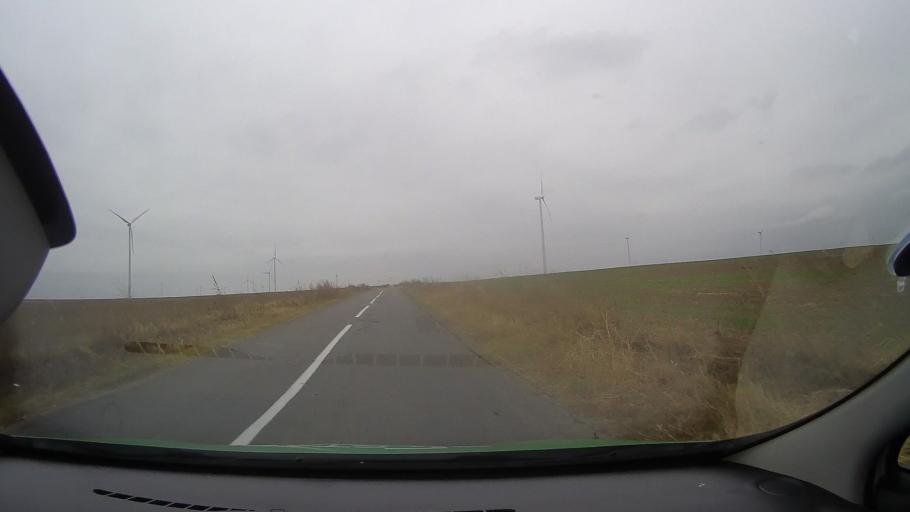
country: RO
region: Constanta
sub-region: Comuna Pantelimon
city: Pantelimon
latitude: 44.5037
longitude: 28.3496
